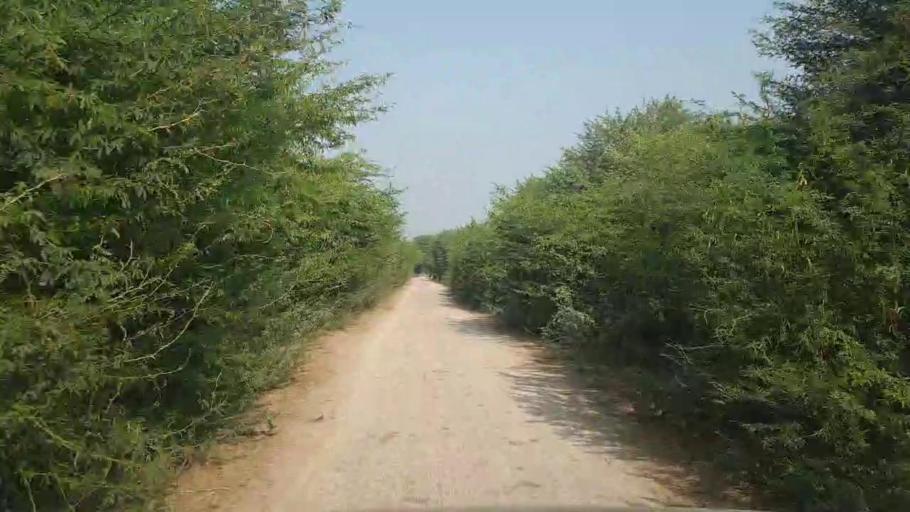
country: PK
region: Sindh
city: Umarkot
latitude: 25.3787
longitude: 69.7287
